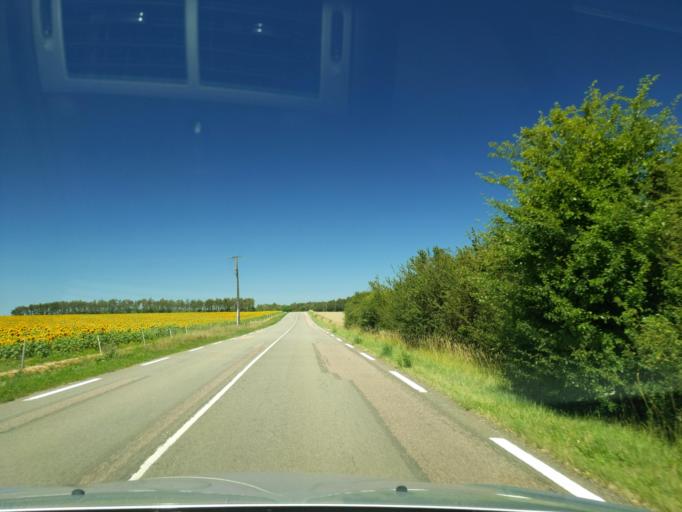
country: FR
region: Bourgogne
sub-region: Departement de la Cote-d'Or
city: Is-sur-Tille
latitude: 47.4991
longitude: 5.0856
